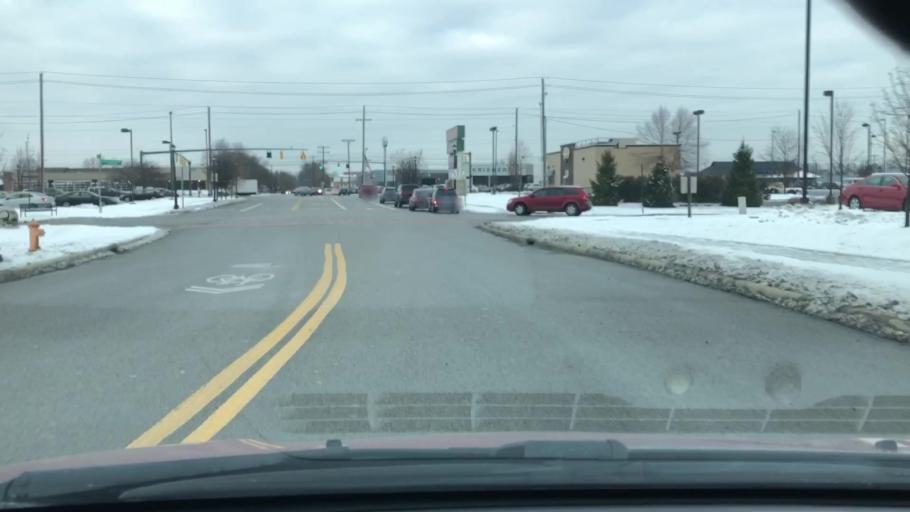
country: US
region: Ohio
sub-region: Franklin County
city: Minerva Park
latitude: 40.0590
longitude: -82.9711
